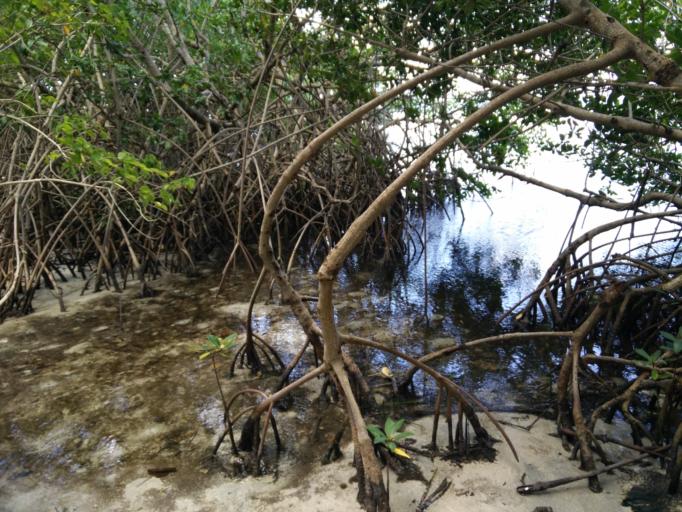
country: GP
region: Guadeloupe
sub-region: Guadeloupe
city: Petit-Canal
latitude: 16.3658
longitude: -61.5068
